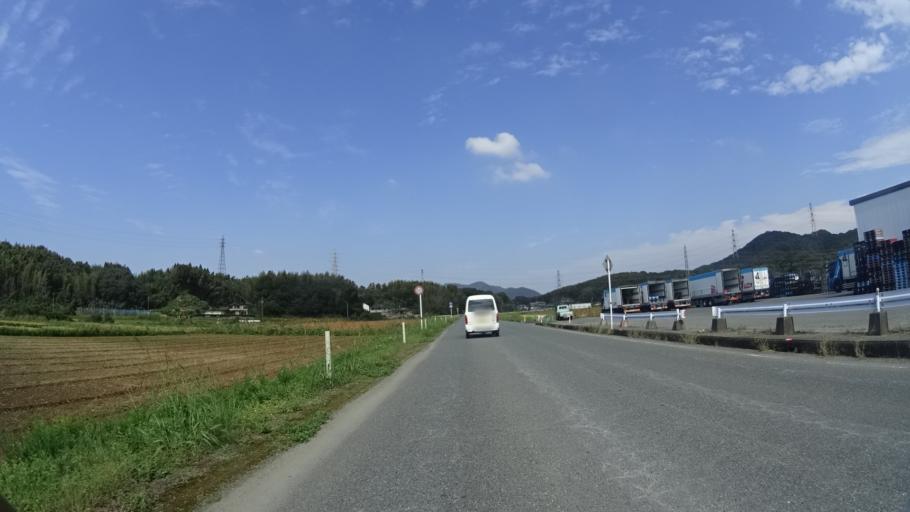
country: JP
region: Kumamoto
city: Matsubase
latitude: 32.6528
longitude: 130.7160
